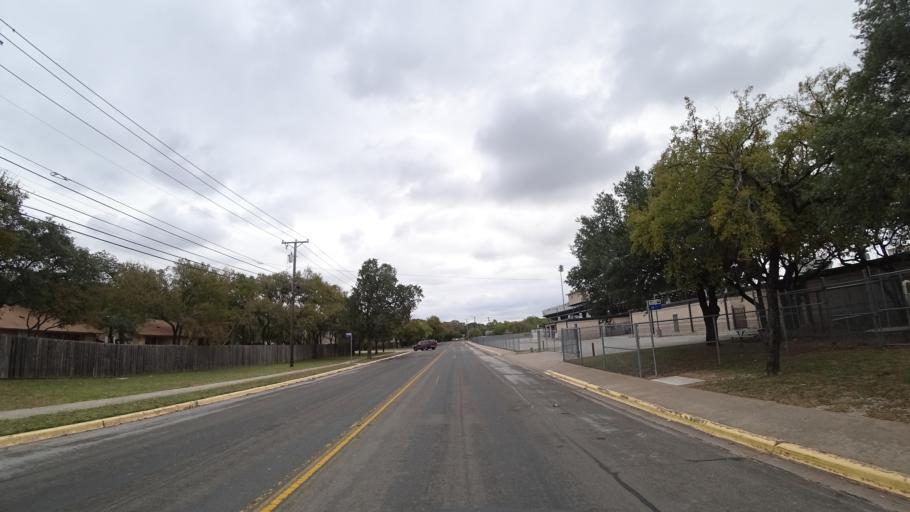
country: US
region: Texas
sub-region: Williamson County
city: Round Rock
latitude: 30.5080
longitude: -97.6946
